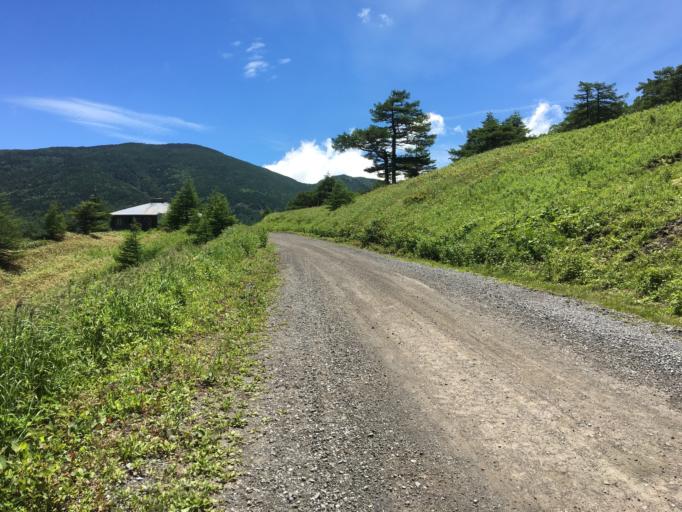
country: JP
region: Nagano
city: Komoro
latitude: 36.4073
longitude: 138.4637
